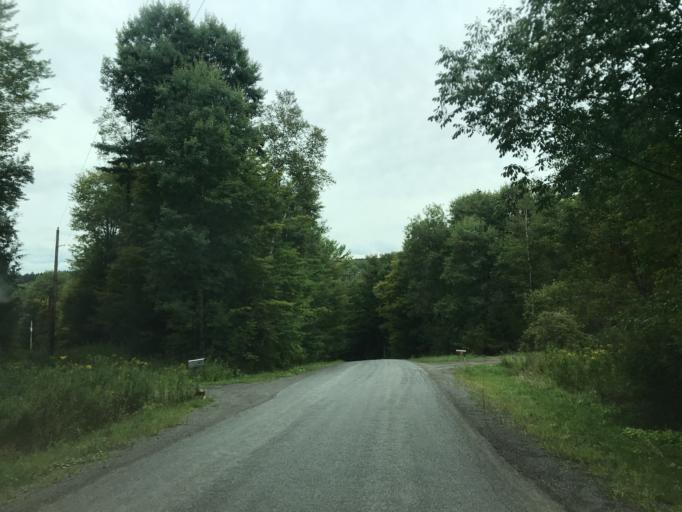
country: US
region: New York
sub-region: Delaware County
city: Stamford
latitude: 42.5146
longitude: -74.6342
